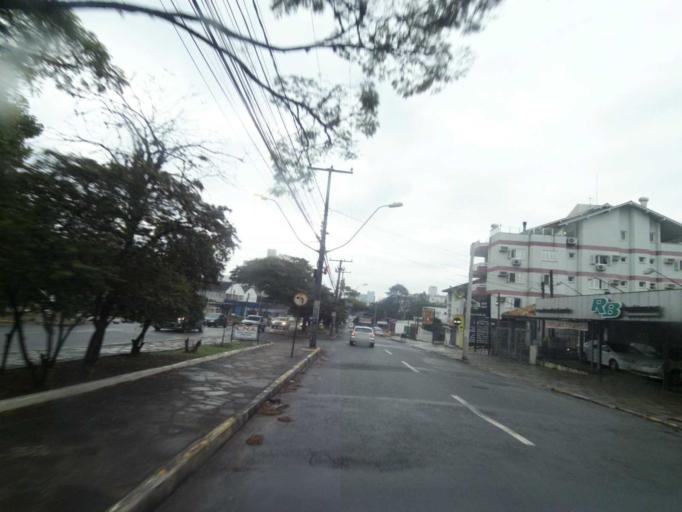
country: BR
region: Rio Grande do Sul
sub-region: Sao Leopoldo
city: Sao Leopoldo
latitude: -29.7693
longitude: -51.1379
